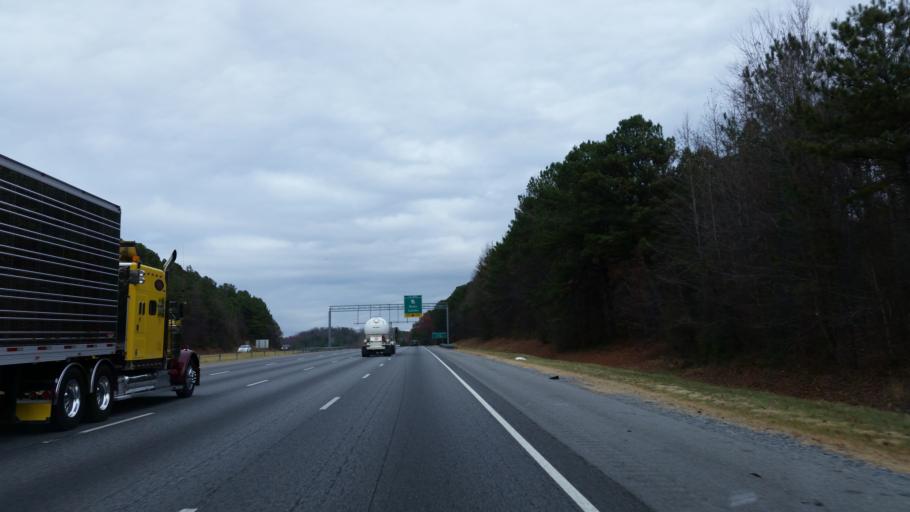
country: US
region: Georgia
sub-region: Bartow County
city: Cartersville
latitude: 34.1946
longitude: -84.7645
